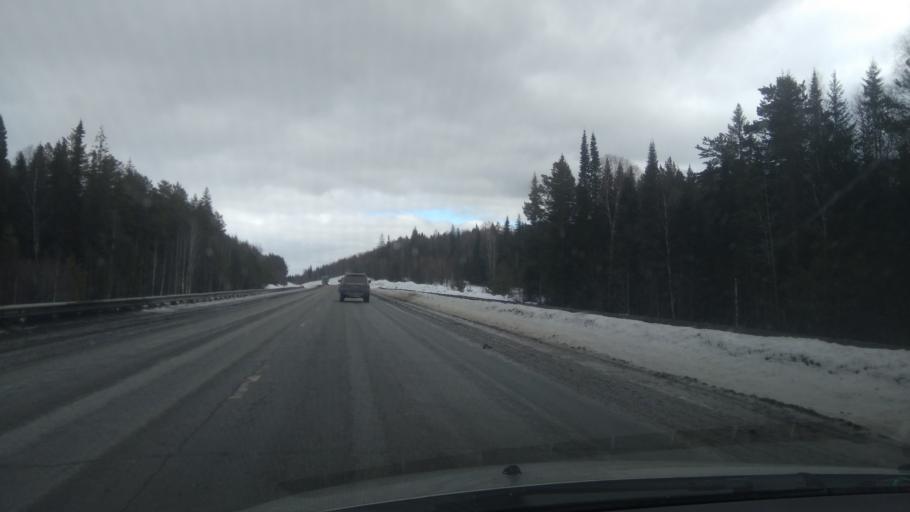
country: RU
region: Sverdlovsk
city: Bisert'
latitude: 56.8272
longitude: 58.9880
